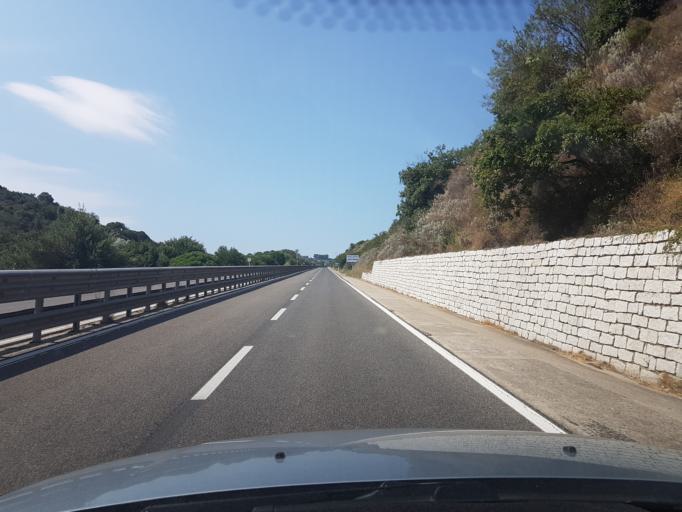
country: IT
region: Sardinia
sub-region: Provincia di Oristano
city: Soddi
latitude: 40.1397
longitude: 8.8710
